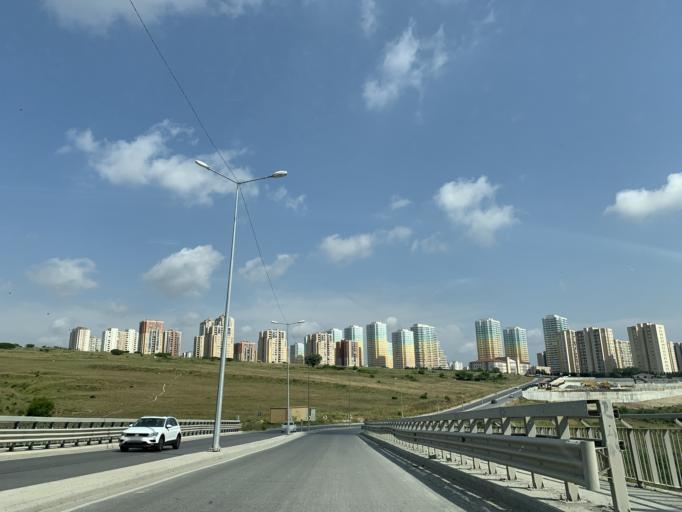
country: TR
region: Istanbul
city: Esenyurt
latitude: 41.0693
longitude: 28.7034
